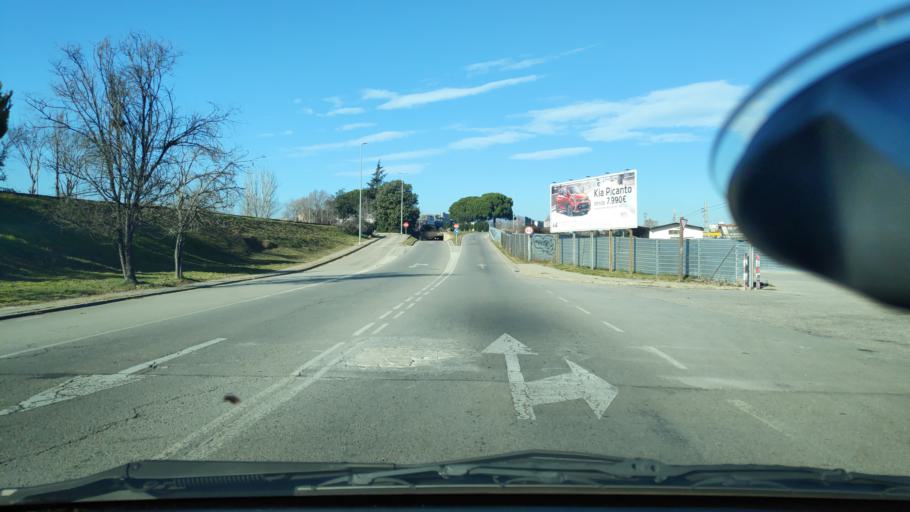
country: ES
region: Catalonia
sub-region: Provincia de Barcelona
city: Sabadell
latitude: 41.5263
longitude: 2.1058
